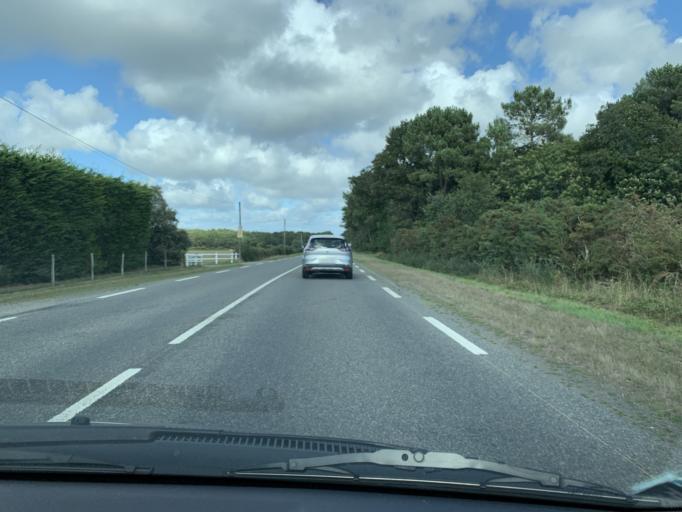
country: FR
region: Pays de la Loire
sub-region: Departement de la Loire-Atlantique
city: Saint-Molf
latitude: 47.3718
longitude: -2.4056
